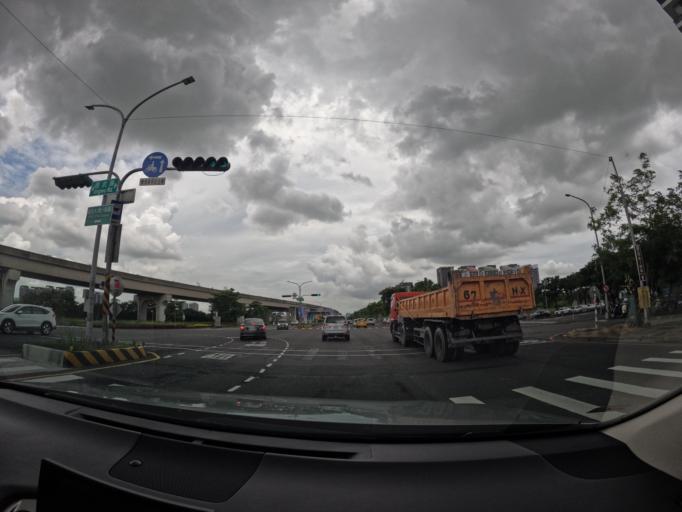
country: TW
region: Taiwan
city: Fengshan
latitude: 22.7432
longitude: 120.3168
